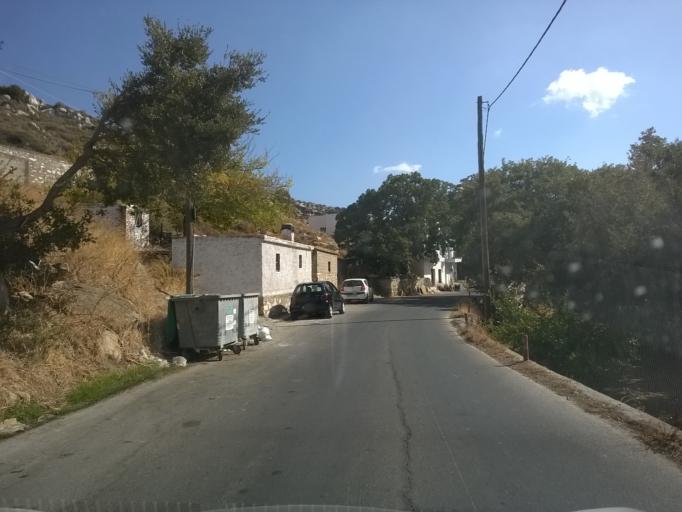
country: GR
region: South Aegean
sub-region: Nomos Kykladon
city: Filotion
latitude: 37.1003
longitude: 25.4814
